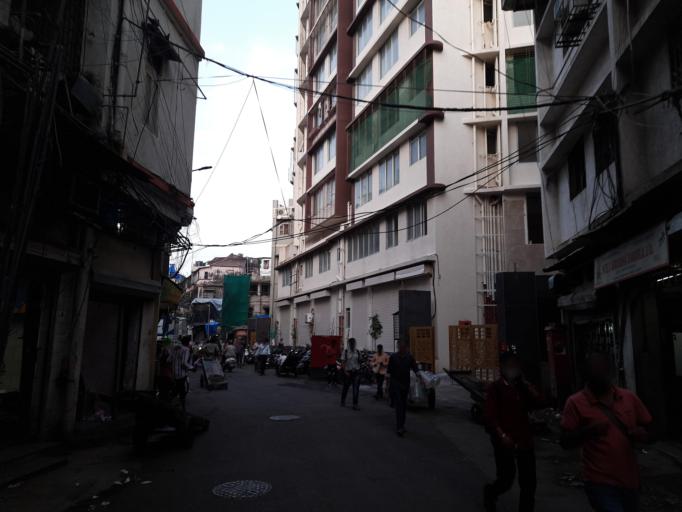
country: IN
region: Maharashtra
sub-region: Raigarh
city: Uran
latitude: 18.9497
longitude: 72.8276
